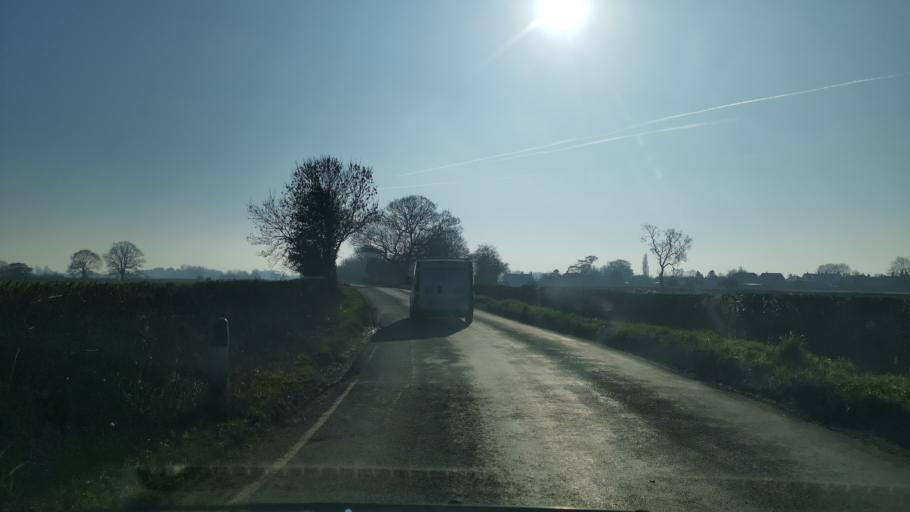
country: GB
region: England
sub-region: City of York
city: Murton
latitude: 53.9713
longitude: -1.0111
